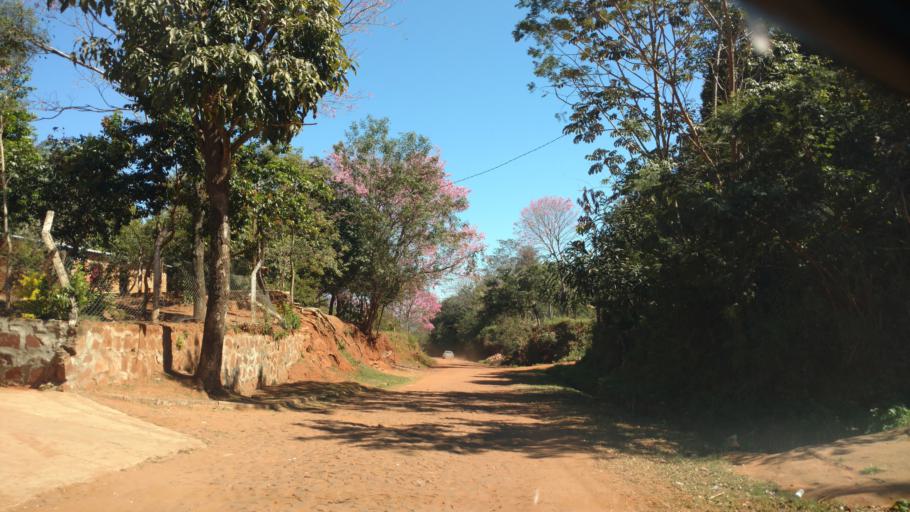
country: PY
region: Paraguari
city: Yaguaron
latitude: -25.5642
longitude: -57.2993
